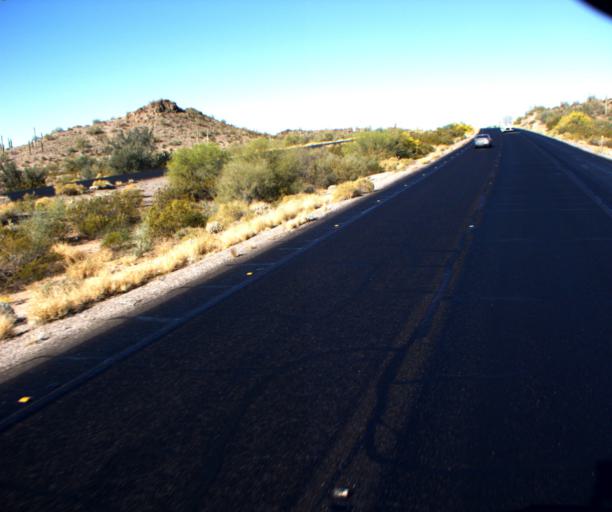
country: US
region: Arizona
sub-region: Pinal County
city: Maricopa
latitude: 32.8487
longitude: -112.3100
